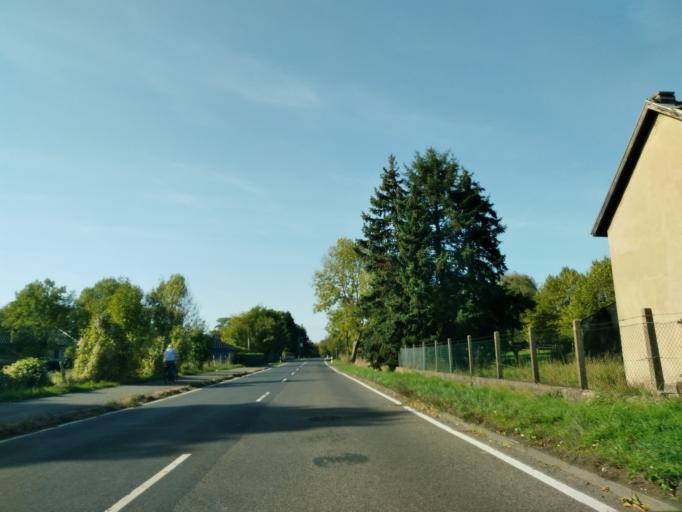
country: DE
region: North Rhine-Westphalia
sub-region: Regierungsbezirk Koln
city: Stossdorf
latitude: 50.7395
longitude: 7.2504
